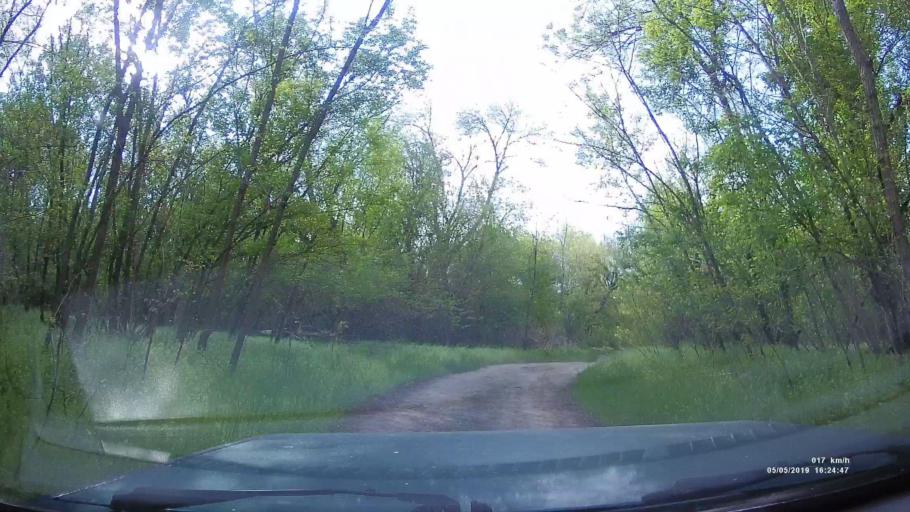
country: RU
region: Rostov
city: Konstantinovsk
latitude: 47.7604
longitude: 41.0249
